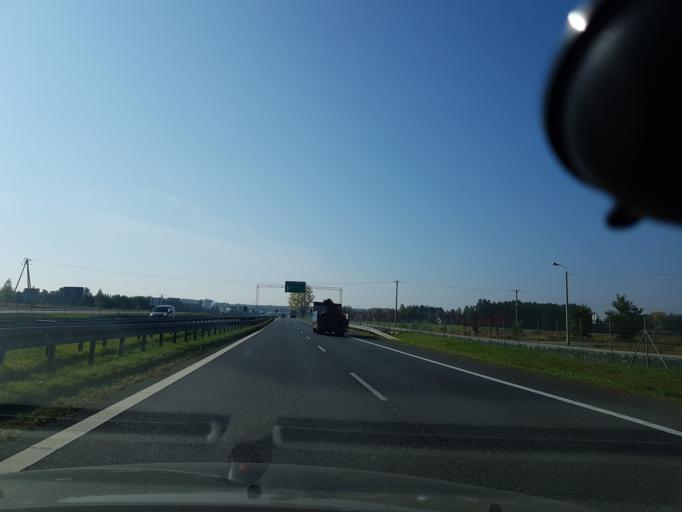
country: PL
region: Masovian Voivodeship
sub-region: Powiat zyrardowski
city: Mszczonow
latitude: 51.9471
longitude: 20.4869
